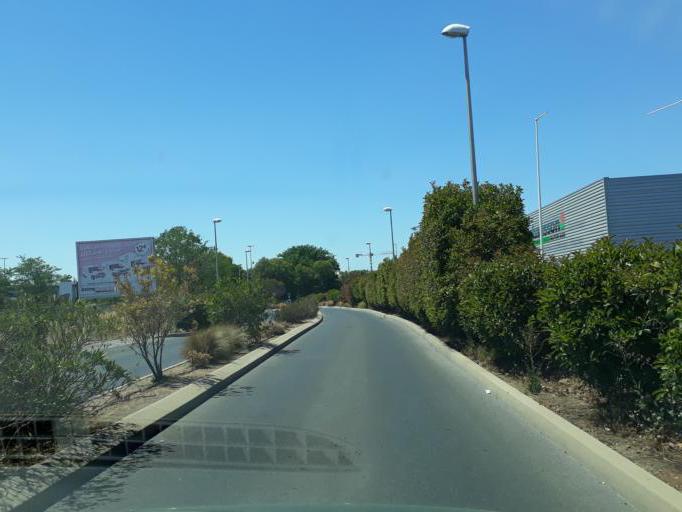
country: FR
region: Languedoc-Roussillon
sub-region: Departement de l'Herault
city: Agde
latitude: 43.3079
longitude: 3.4940
